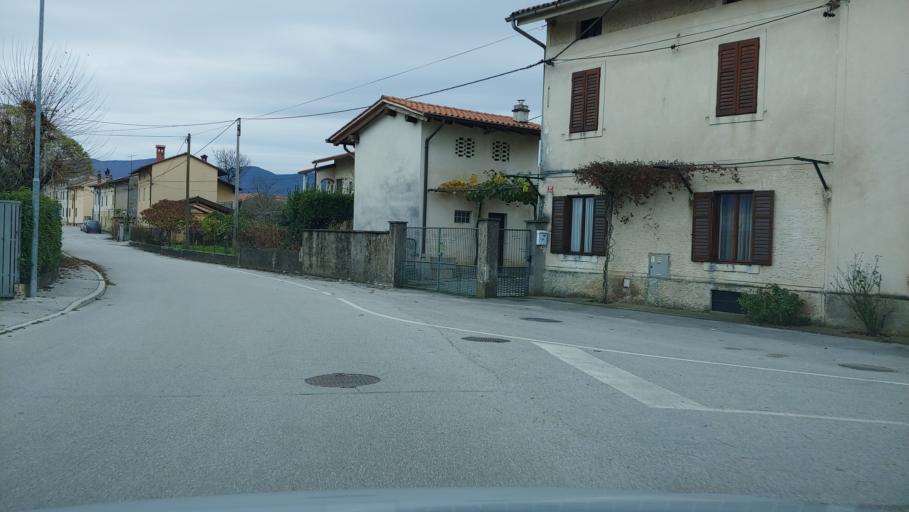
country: SI
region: Sempeter-Vrtojba
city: Vrtojba
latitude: 45.9118
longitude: 13.6303
